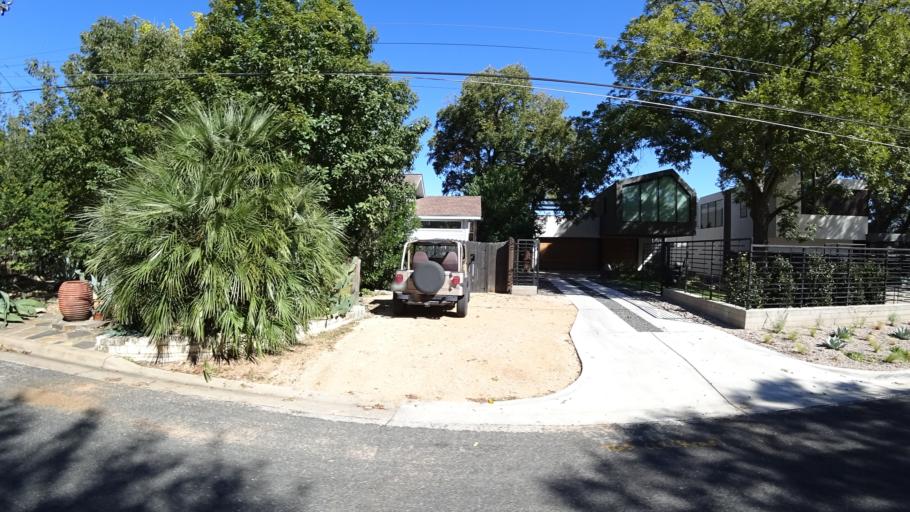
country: US
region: Texas
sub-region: Travis County
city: Austin
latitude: 30.2440
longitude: -97.7607
